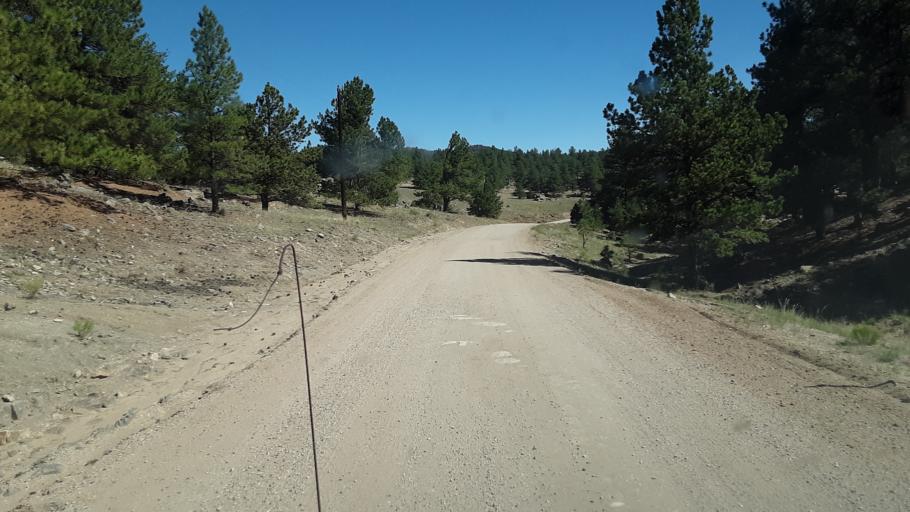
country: US
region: Colorado
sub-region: Custer County
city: Westcliffe
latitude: 38.2092
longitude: -105.4436
